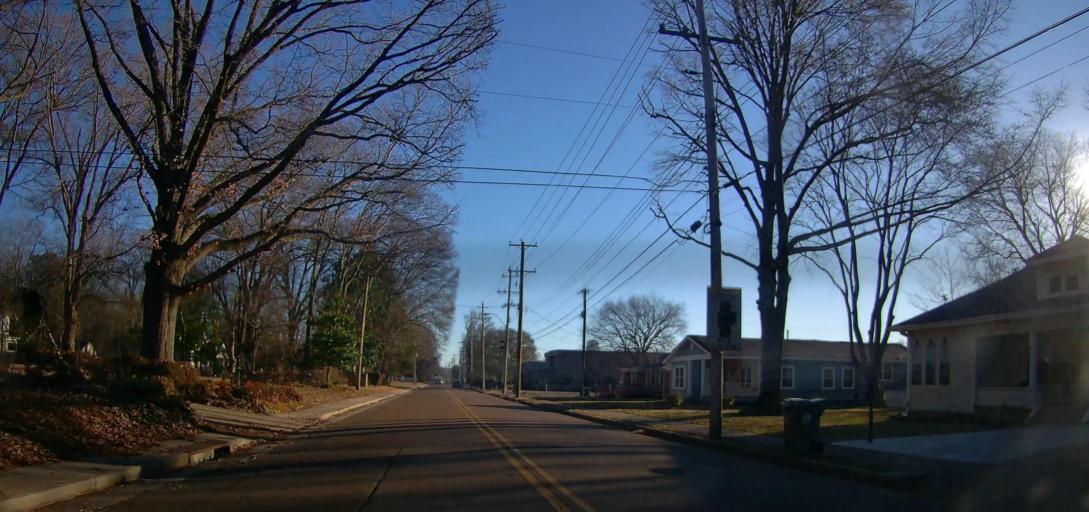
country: US
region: Tennessee
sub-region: Shelby County
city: Millington
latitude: 35.3489
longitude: -89.8955
